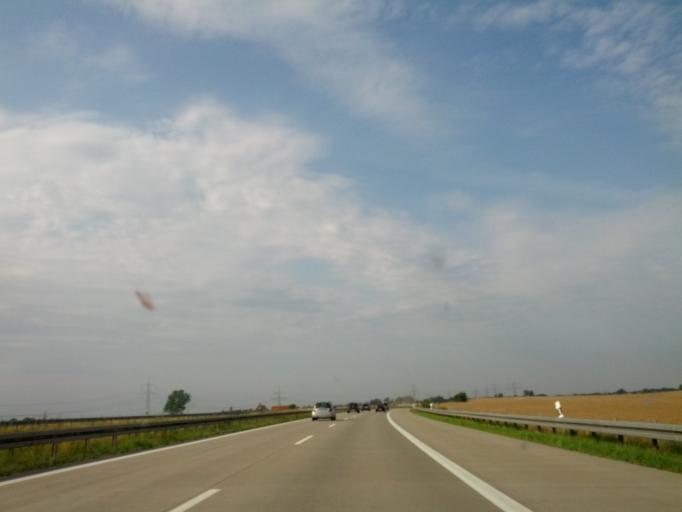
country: DE
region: Mecklenburg-Vorpommern
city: Kavelstorf
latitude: 53.9828
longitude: 12.1962
